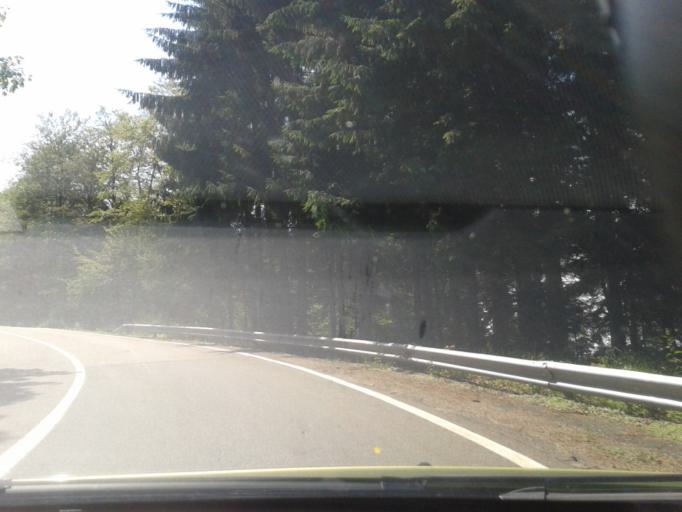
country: RO
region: Sibiu
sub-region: Comuna Cartisoara
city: Cartisoara
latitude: 45.6672
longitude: 24.5926
